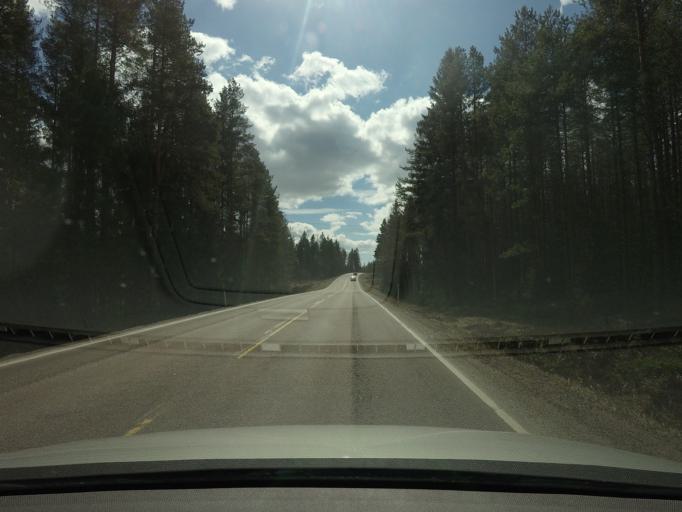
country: FI
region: Kymenlaakso
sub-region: Kotka-Hamina
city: Hamina
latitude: 60.6662
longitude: 27.2681
